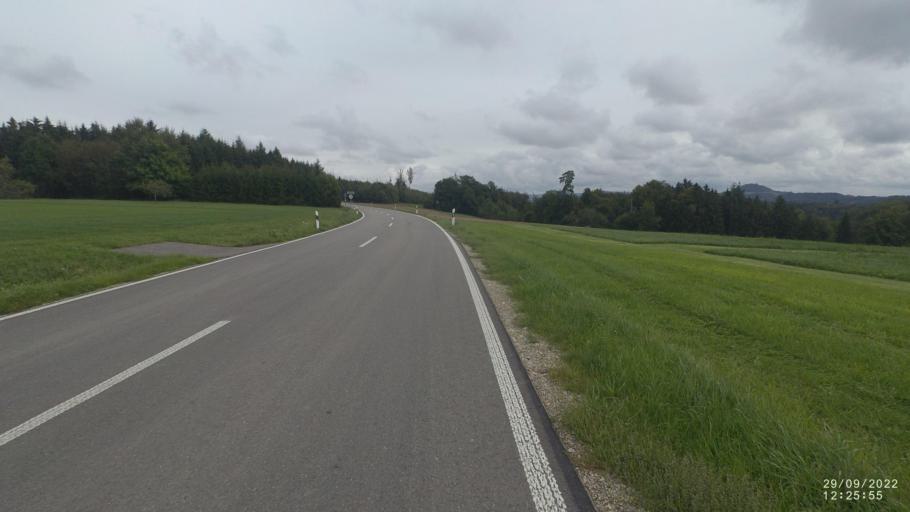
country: DE
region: Baden-Wuerttemberg
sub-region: Regierungsbezirk Stuttgart
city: Bortlingen
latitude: 48.7713
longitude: 9.6426
